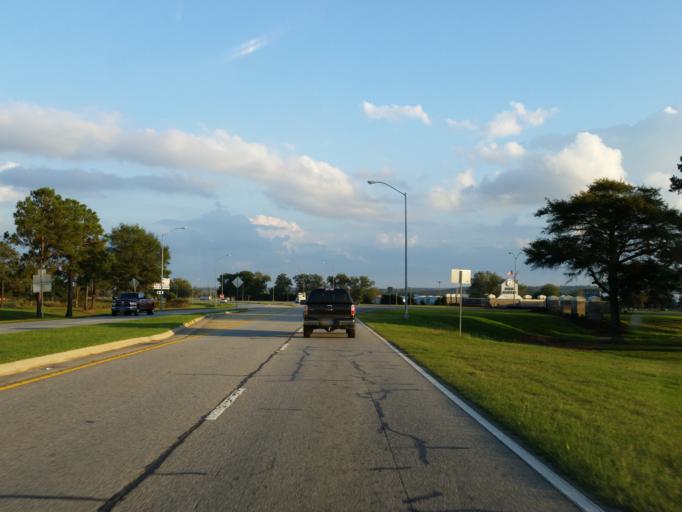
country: US
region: Georgia
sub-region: Houston County
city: Perry
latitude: 32.4447
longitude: -83.7500
